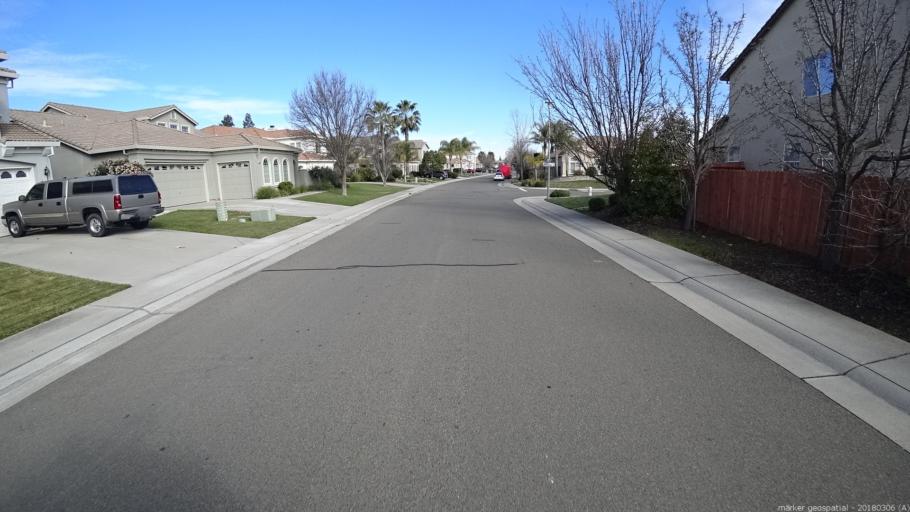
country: US
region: California
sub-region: Sacramento County
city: Vineyard
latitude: 38.4729
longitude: -121.3105
